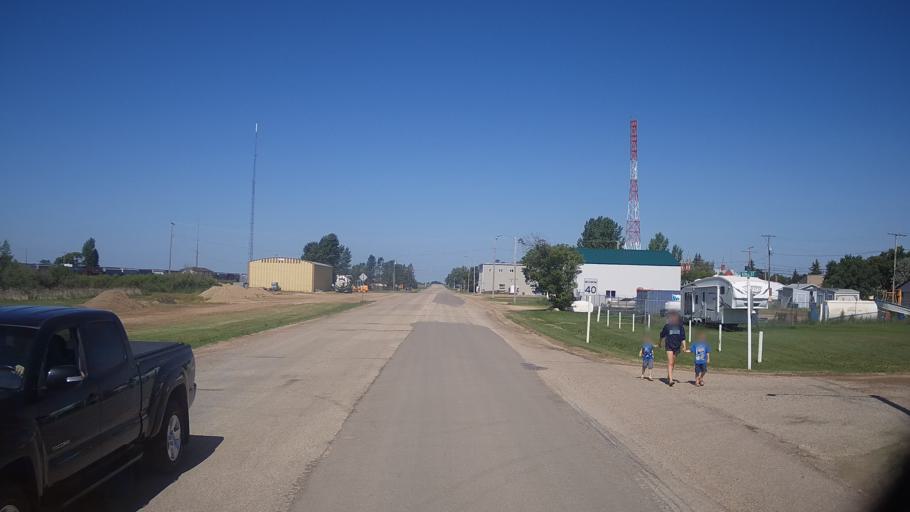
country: CA
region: Saskatchewan
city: Saskatoon
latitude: 51.8923
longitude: -106.0540
